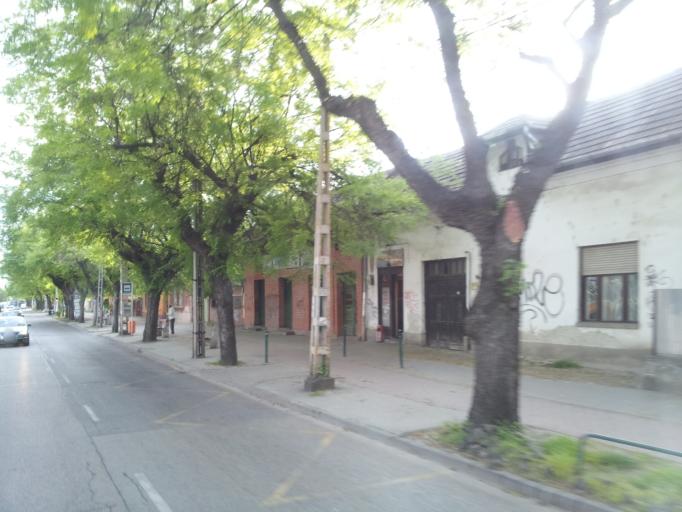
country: HU
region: Budapest
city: Budapest XV. keruelet
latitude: 47.5677
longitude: 19.1251
